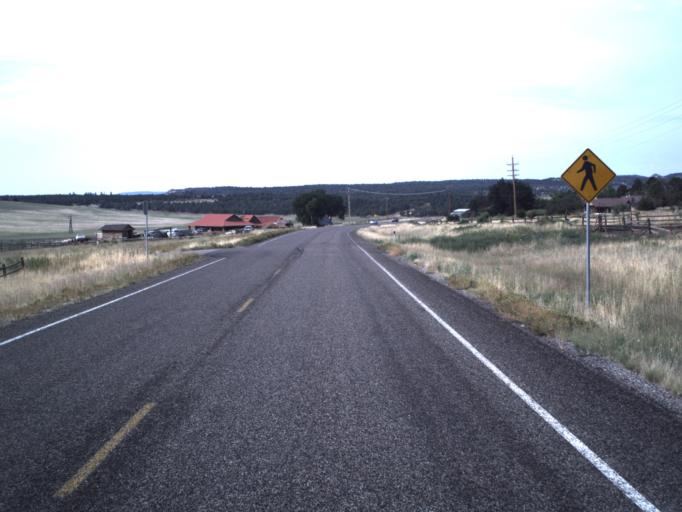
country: US
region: Utah
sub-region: Washington County
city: Hildale
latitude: 37.2488
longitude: -112.8014
